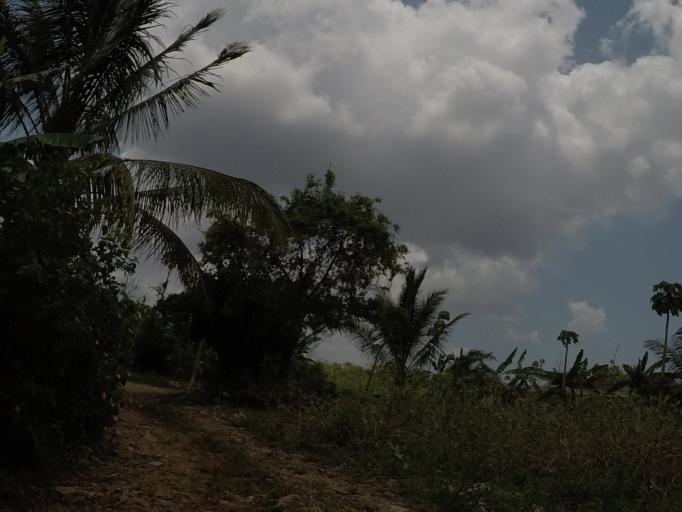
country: TZ
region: Zanzibar Central/South
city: Koani
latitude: -6.1720
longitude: 39.3089
